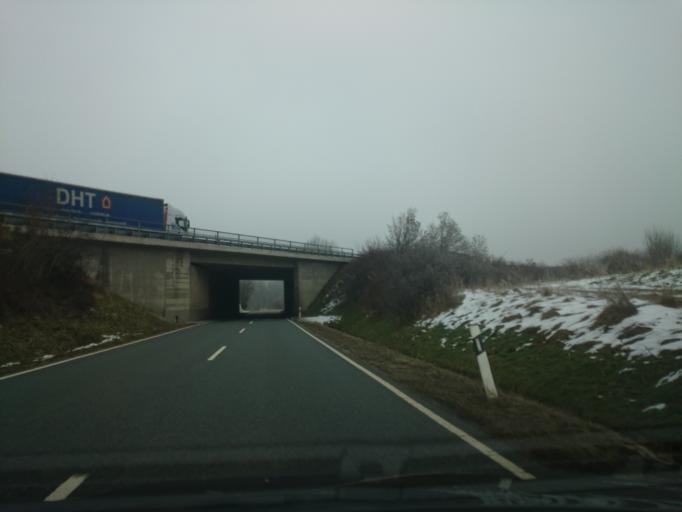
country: DE
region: Bavaria
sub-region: Regierungsbezirk Mittelfranken
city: Thalmassing
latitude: 49.1046
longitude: 11.2827
